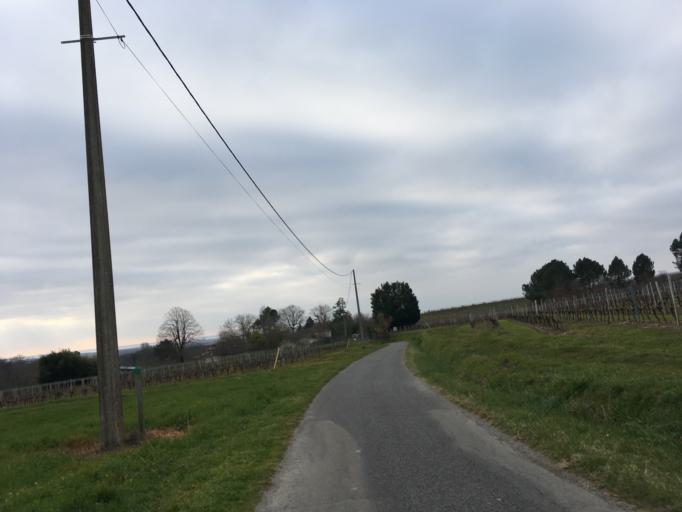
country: FR
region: Aquitaine
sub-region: Departement de la Gironde
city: Saint-Ciers-sur-Gironde
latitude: 45.3095
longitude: -0.6100
